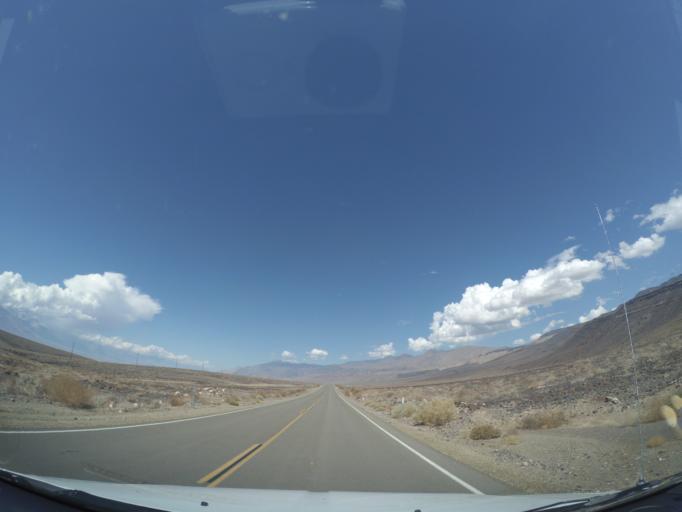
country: US
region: California
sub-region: Inyo County
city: Lone Pine
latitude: 36.4003
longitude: -117.8092
